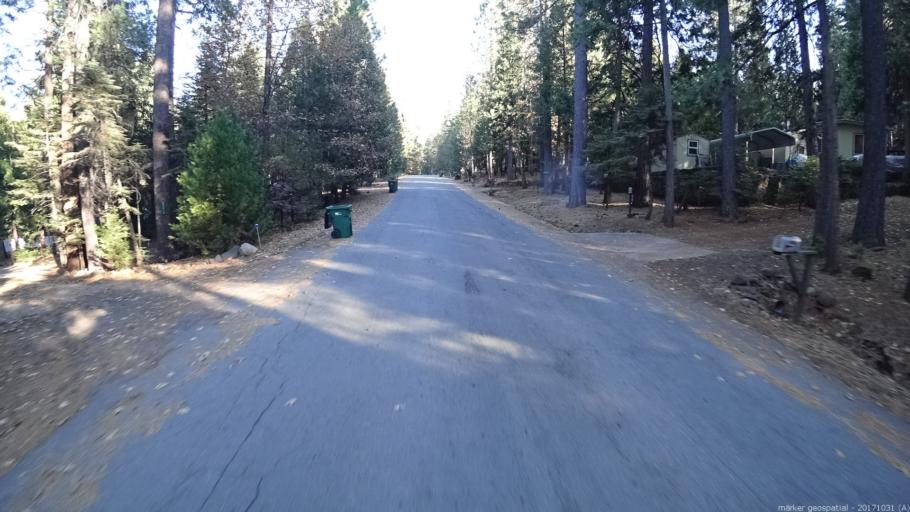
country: US
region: California
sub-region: Shasta County
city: Shingletown
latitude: 40.4974
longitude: -121.9071
